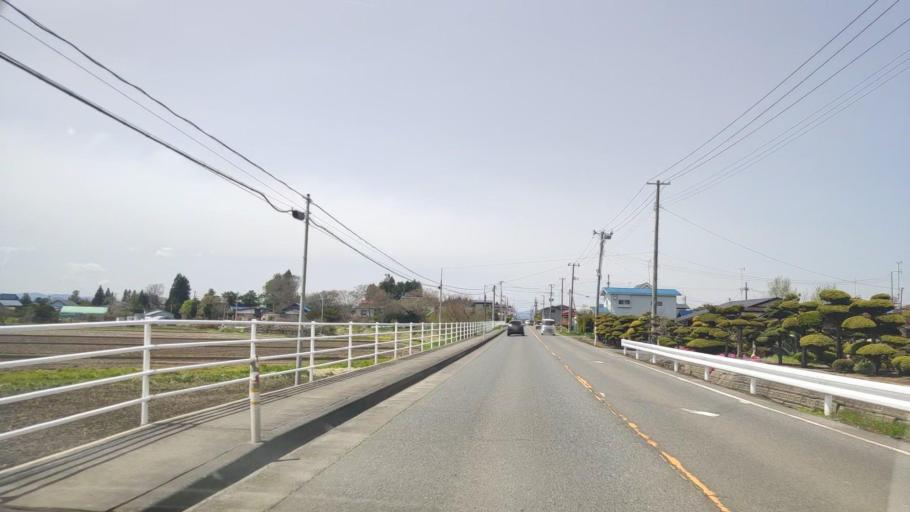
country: JP
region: Aomori
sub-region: Misawa Shi
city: Inuotose
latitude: 40.6007
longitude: 141.3069
